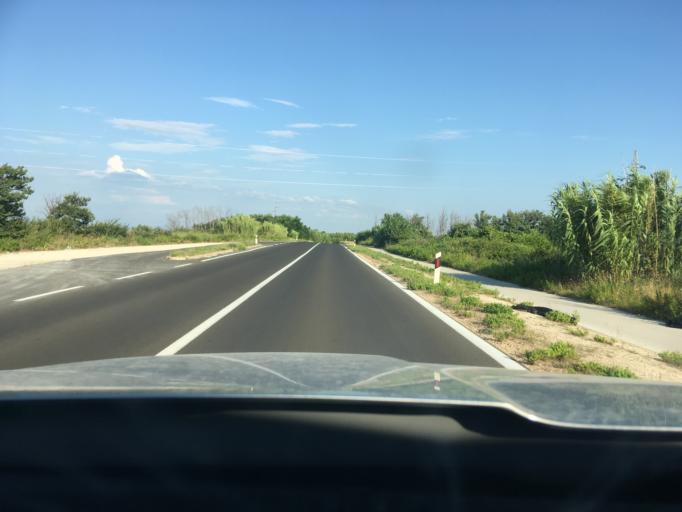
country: HR
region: Zadarska
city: Privlaka
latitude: 44.2673
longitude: 15.1408
